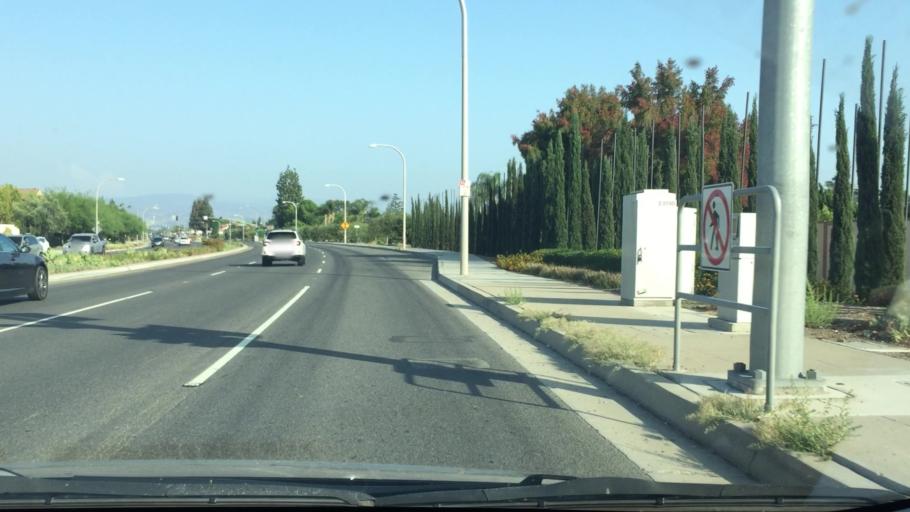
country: US
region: California
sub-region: Orange County
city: Placentia
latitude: 33.9084
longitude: -117.8509
